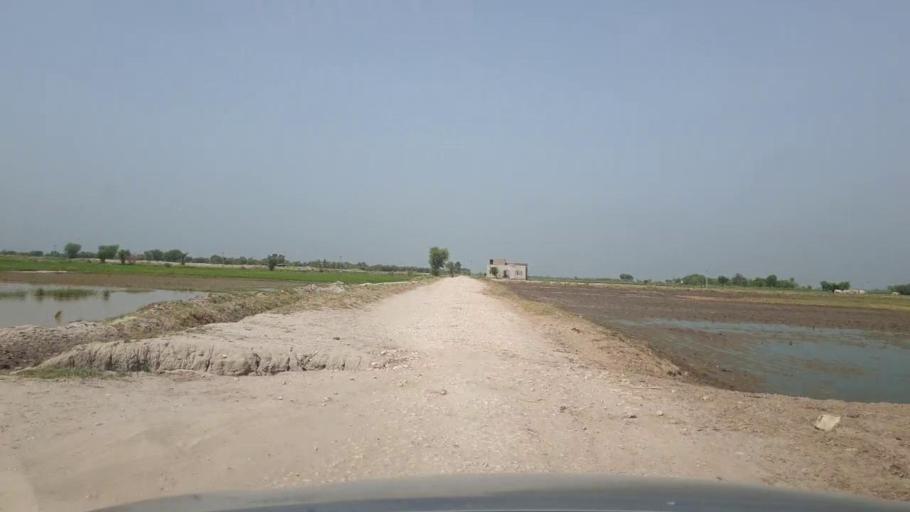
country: PK
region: Sindh
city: Garhi Yasin
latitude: 27.9115
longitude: 68.4059
